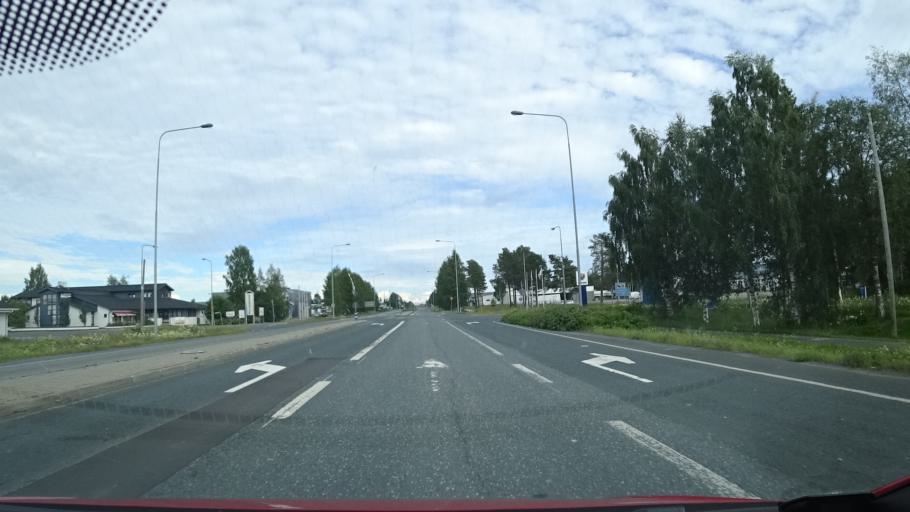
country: FI
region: Lapland
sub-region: Kemi-Tornio
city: Keminmaa
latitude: 65.8006
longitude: 24.4984
